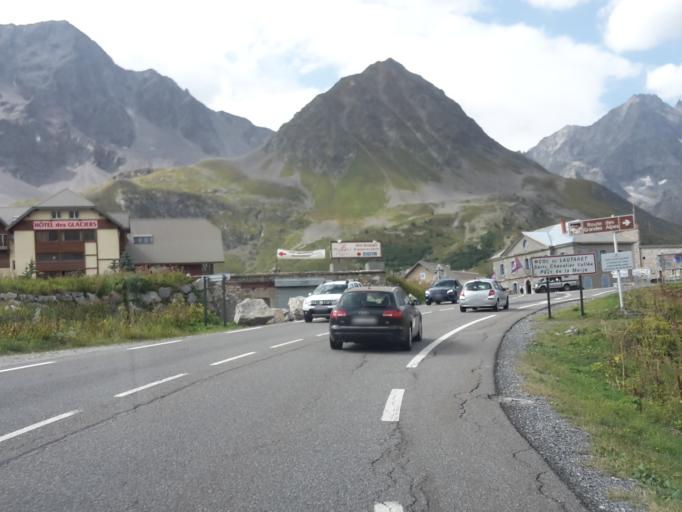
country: FR
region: Provence-Alpes-Cote d'Azur
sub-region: Departement des Hautes-Alpes
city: Le Monetier-les-Bains
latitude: 45.0362
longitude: 6.4060
